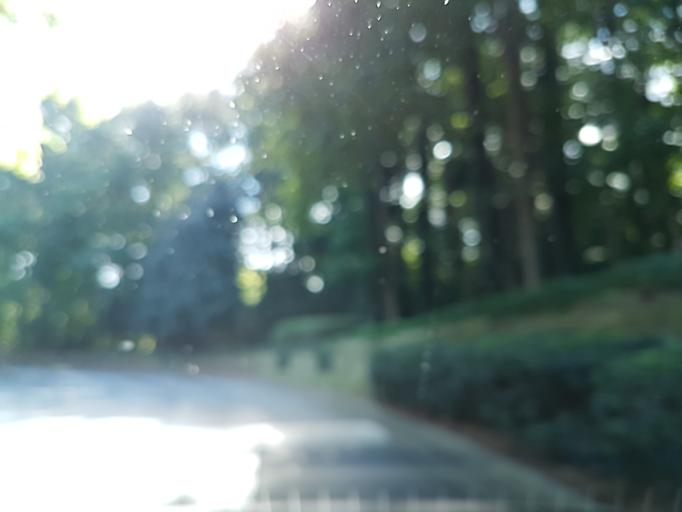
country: US
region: Georgia
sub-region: DeKalb County
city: North Druid Hills
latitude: 33.8100
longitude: -84.2930
